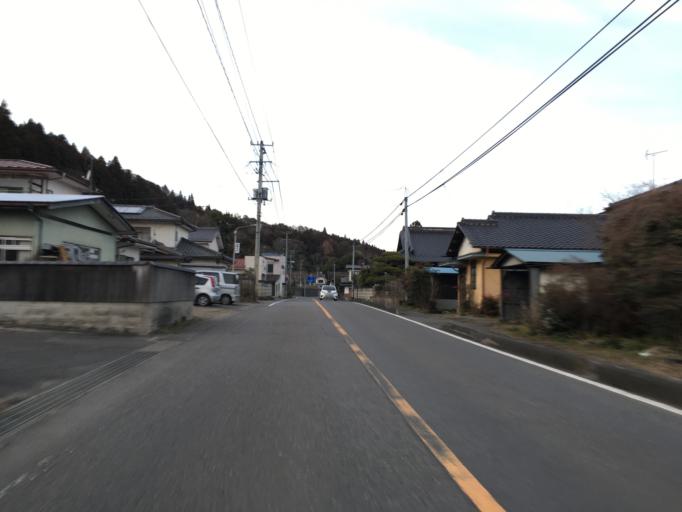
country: JP
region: Ibaraki
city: Daigo
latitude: 36.9021
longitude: 140.4067
